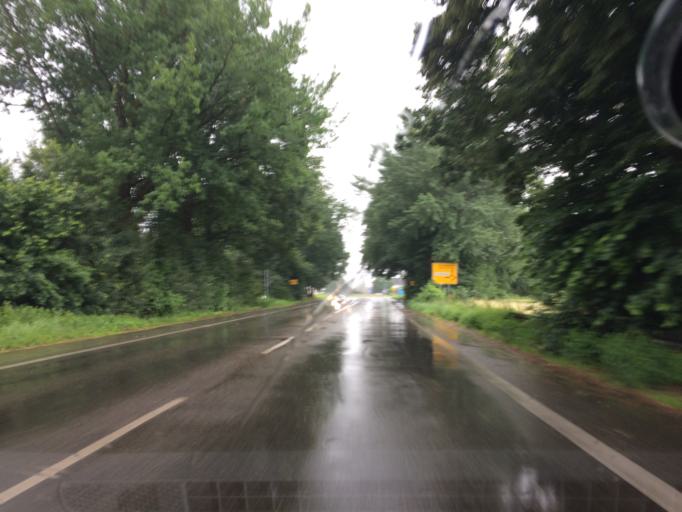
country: DE
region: North Rhine-Westphalia
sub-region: Regierungsbezirk Munster
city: Haltern
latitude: 51.7539
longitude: 7.1936
